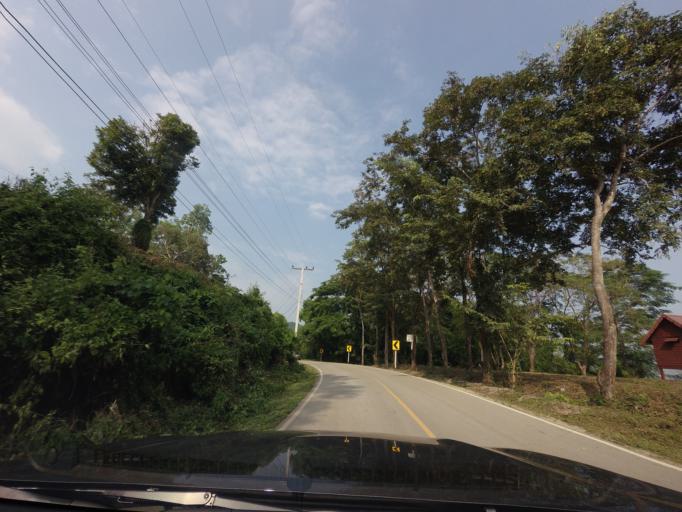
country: TH
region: Loei
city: Chiang Khan
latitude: 17.8466
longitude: 101.5914
